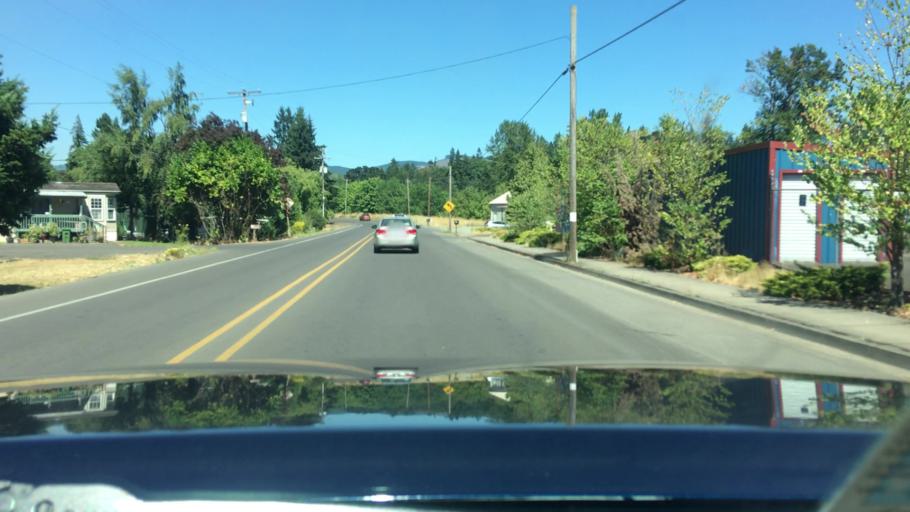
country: US
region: Oregon
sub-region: Lane County
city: Cottage Grove
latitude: 43.8063
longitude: -123.0531
